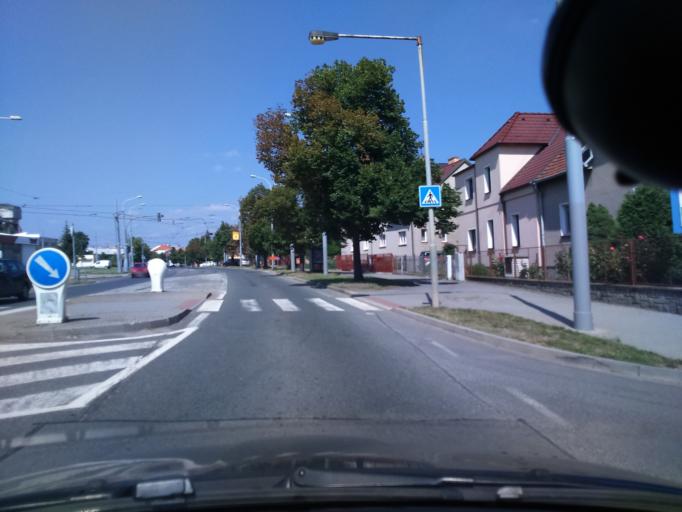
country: CZ
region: Plzensky
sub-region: Okres Plzen-Mesto
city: Pilsen
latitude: 49.7276
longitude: 13.4132
